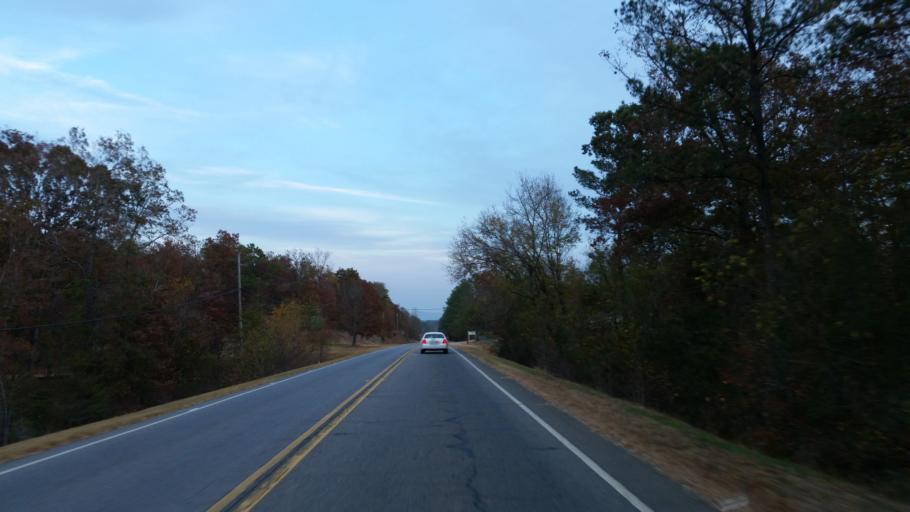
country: US
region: Georgia
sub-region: Murray County
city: Chatsworth
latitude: 34.6049
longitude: -84.8023
